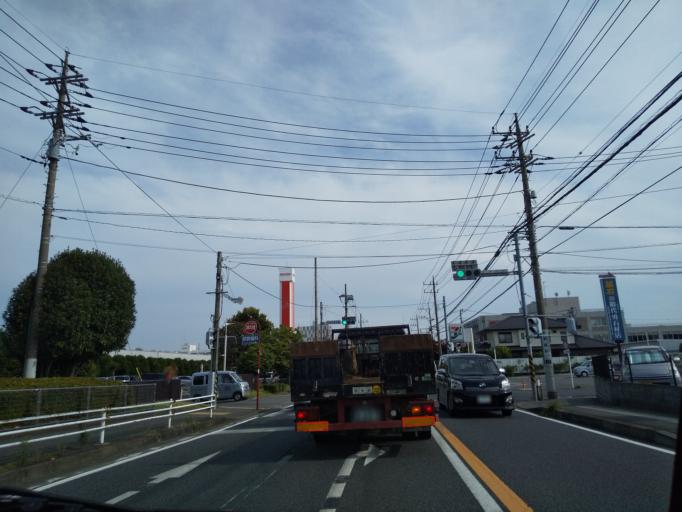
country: JP
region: Kanagawa
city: Zama
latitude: 35.4910
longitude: 139.3400
